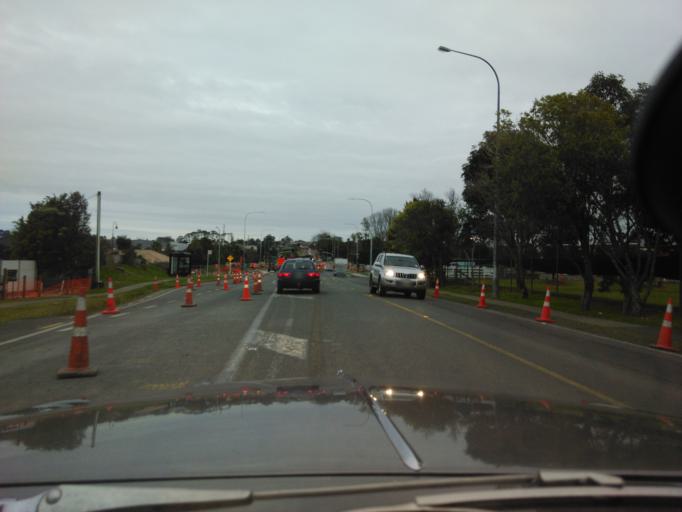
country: NZ
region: Auckland
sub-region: Auckland
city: Rothesay Bay
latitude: -36.7410
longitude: 174.6926
